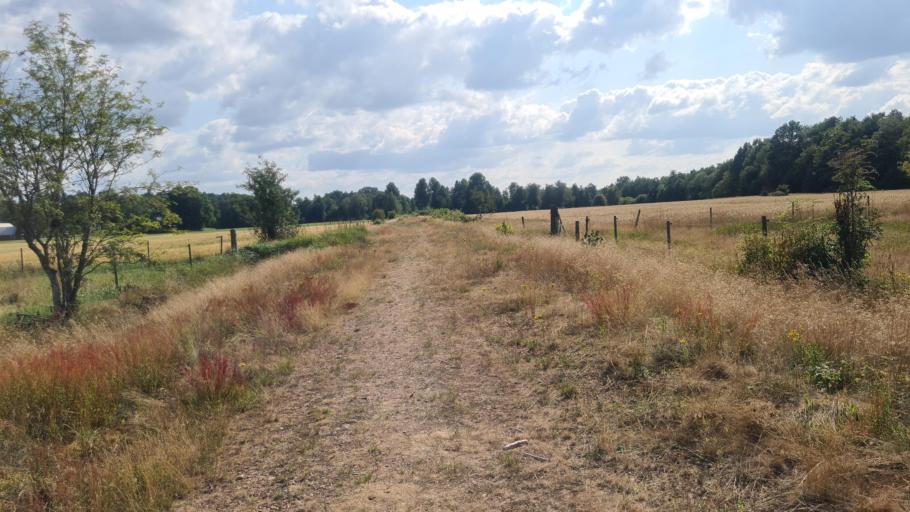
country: SE
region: Kronoberg
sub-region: Ljungby Kommun
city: Ljungby
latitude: 56.7448
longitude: 13.8787
